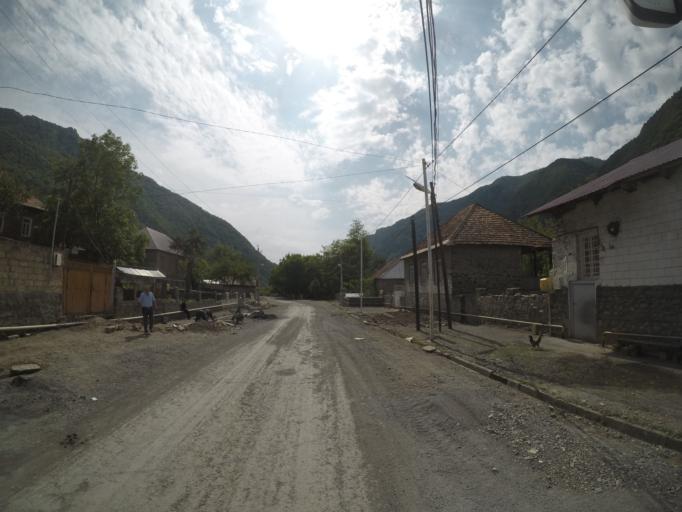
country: AZ
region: Qakh Rayon
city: Qaxbas
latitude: 41.4678
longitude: 47.0525
